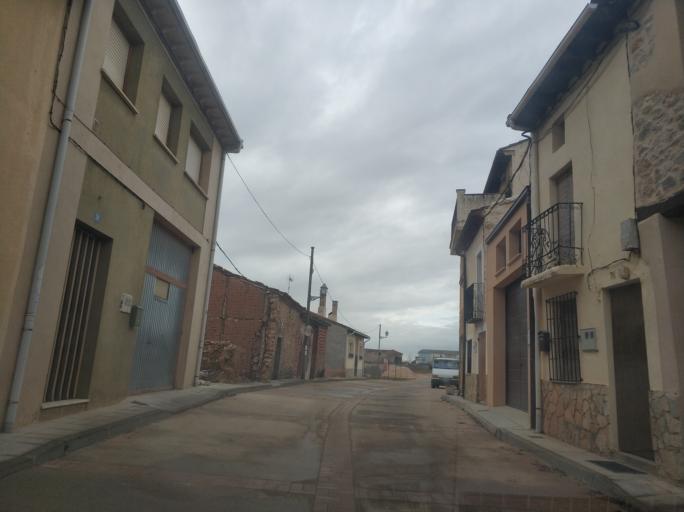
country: ES
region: Castille and Leon
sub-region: Provincia de Soria
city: Alcubilla de Avellaneda
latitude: 41.7246
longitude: -3.3056
